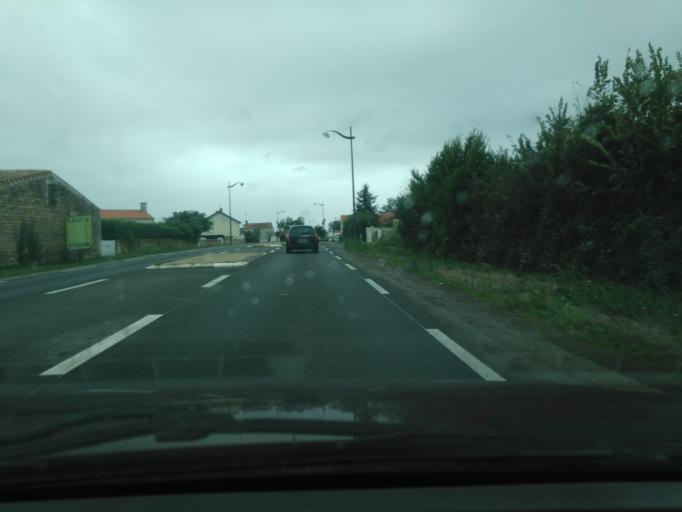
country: FR
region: Pays de la Loire
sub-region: Departement de la Vendee
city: Sainte-Gemme-la-Plaine
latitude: 46.4767
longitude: -1.1115
